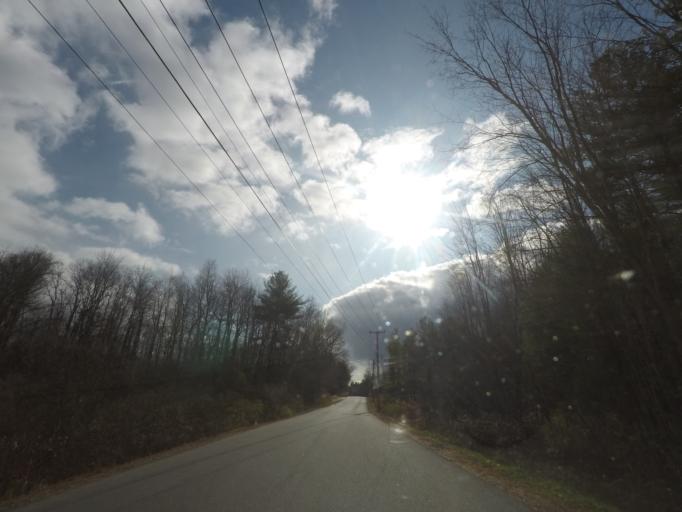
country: US
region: New York
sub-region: Saratoga County
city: Country Knolls
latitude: 42.9261
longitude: -73.8370
